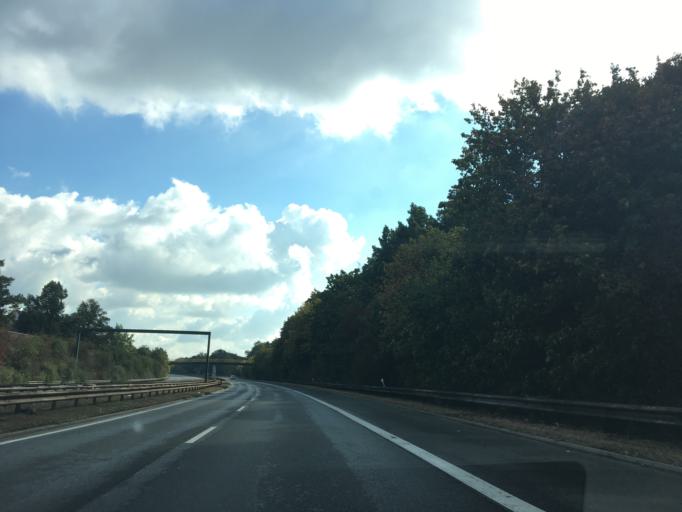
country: DE
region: North Rhine-Westphalia
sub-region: Regierungsbezirk Dusseldorf
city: Dusseldorf
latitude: 51.1882
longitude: 6.7899
